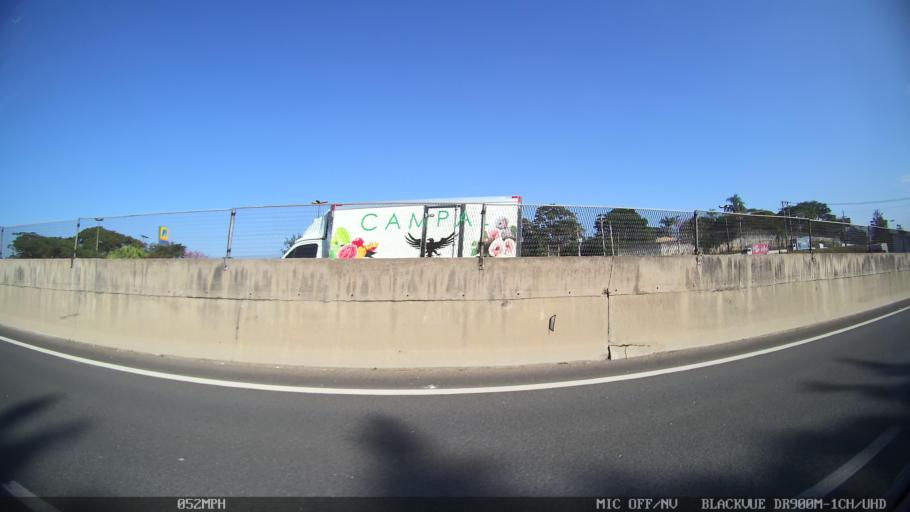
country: BR
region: Sao Paulo
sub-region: Louveira
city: Louveira
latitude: -23.1481
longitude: -46.9364
